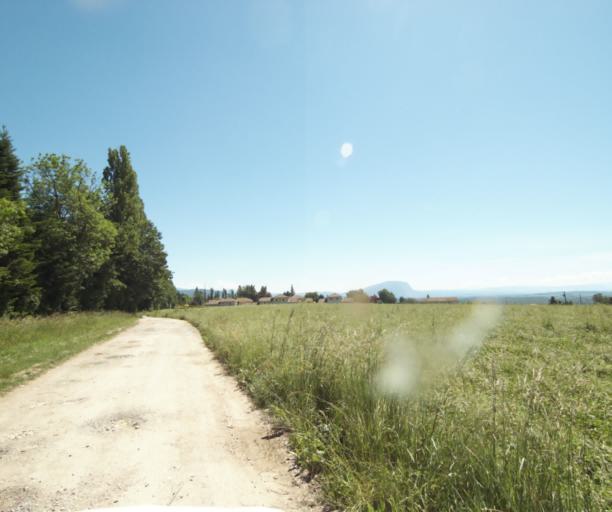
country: FR
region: Rhone-Alpes
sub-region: Departement de la Haute-Savoie
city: Loisin
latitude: 46.2807
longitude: 6.3250
